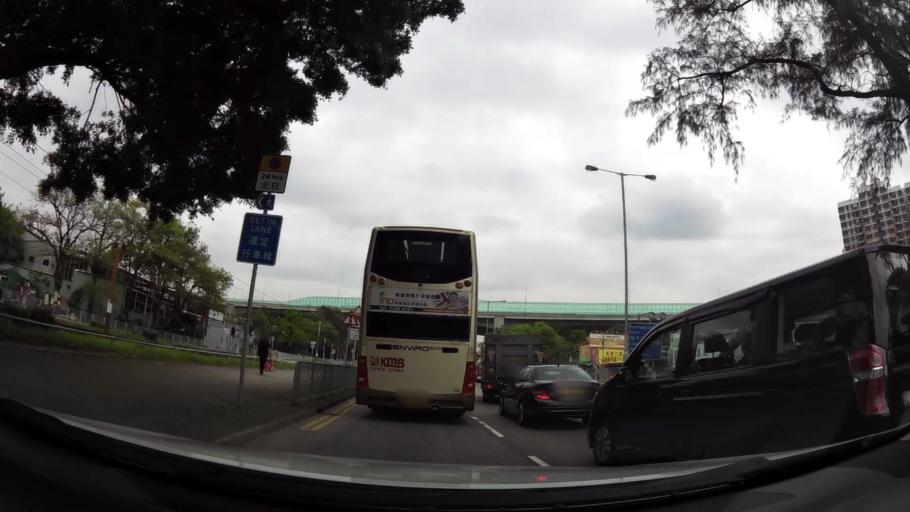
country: HK
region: Tuen Mun
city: Tuen Mun
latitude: 22.4208
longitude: 113.9838
